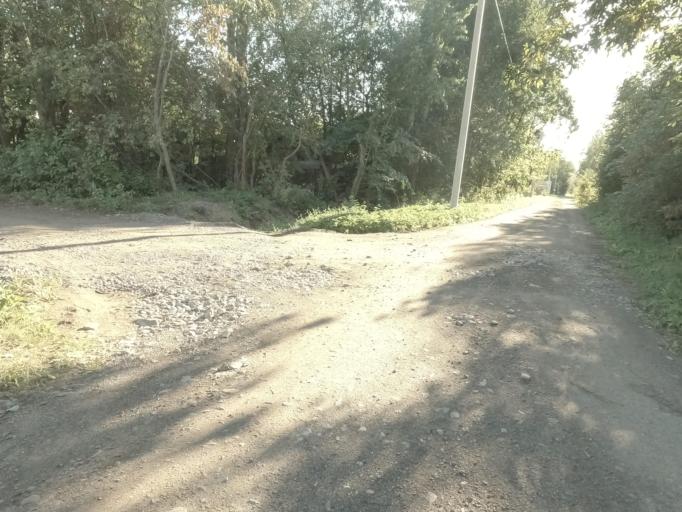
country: RU
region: Leningrad
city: Kirovsk
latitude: 59.9278
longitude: 30.9819
